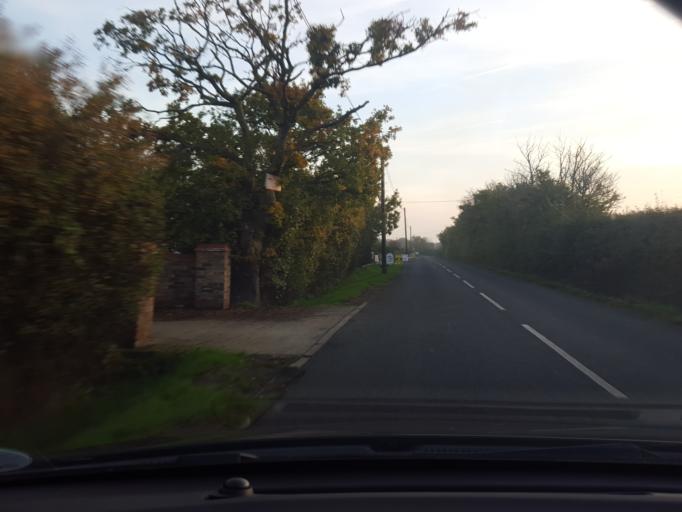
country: GB
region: England
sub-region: Essex
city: Little Clacton
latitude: 51.8253
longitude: 1.1620
